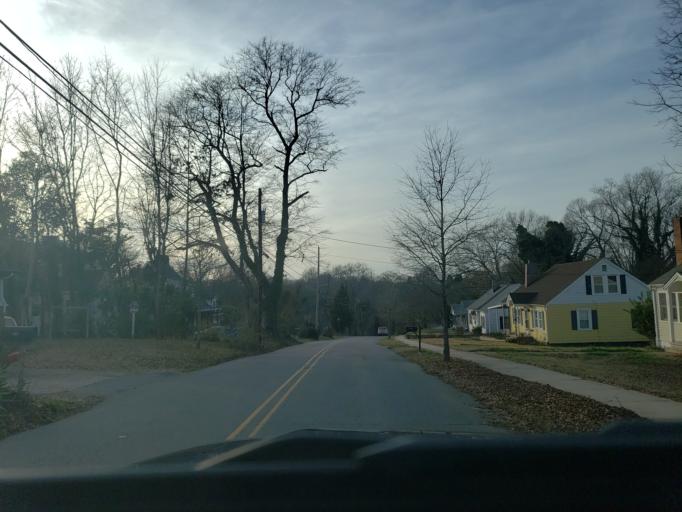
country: US
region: North Carolina
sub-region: Cleveland County
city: Shelby
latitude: 35.2892
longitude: -81.5291
